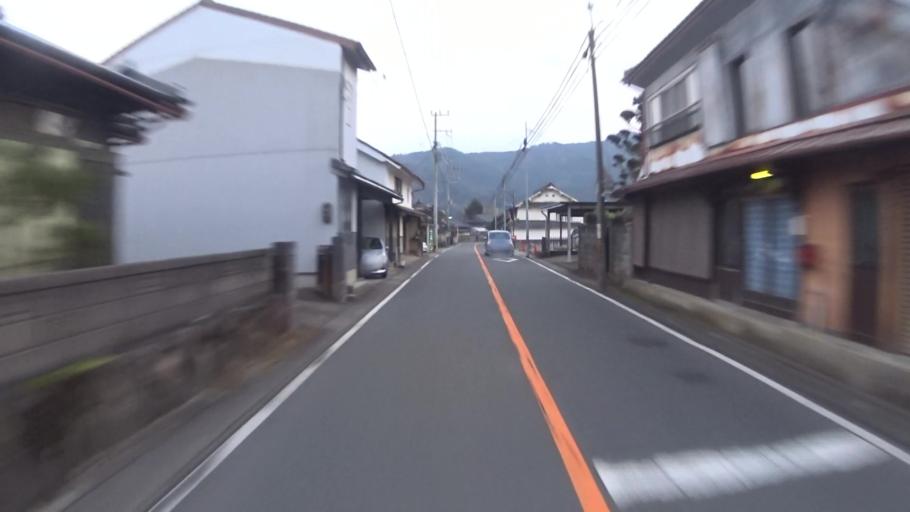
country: JP
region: Kyoto
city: Ayabe
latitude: 35.2984
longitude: 135.3165
